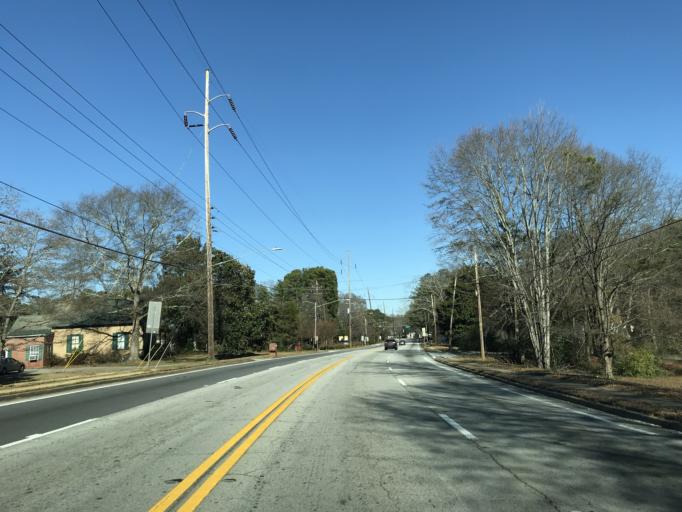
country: US
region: Georgia
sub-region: DeKalb County
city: Tucker
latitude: 33.8672
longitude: -84.2180
